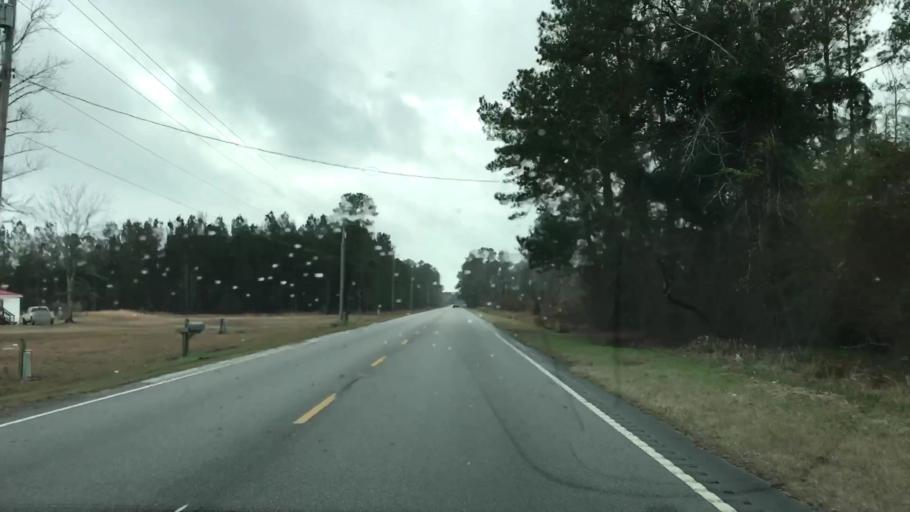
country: US
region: South Carolina
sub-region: Horry County
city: Socastee
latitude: 33.7336
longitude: -79.0826
